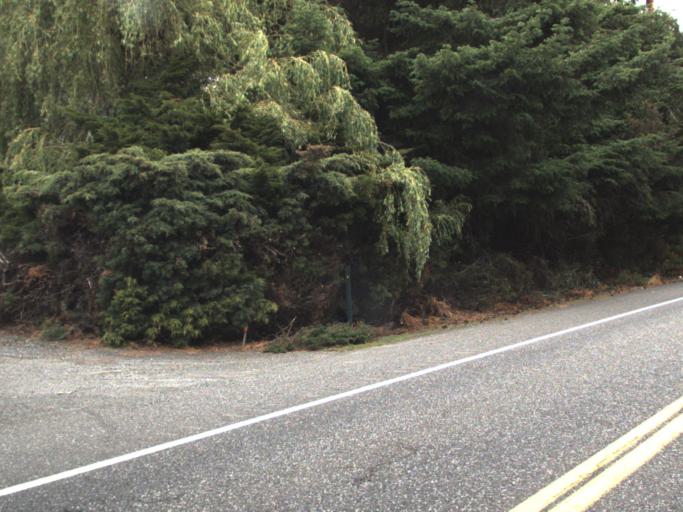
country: US
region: Washington
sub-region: Whatcom County
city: Birch Bay
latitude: 48.8921
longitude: -122.6830
